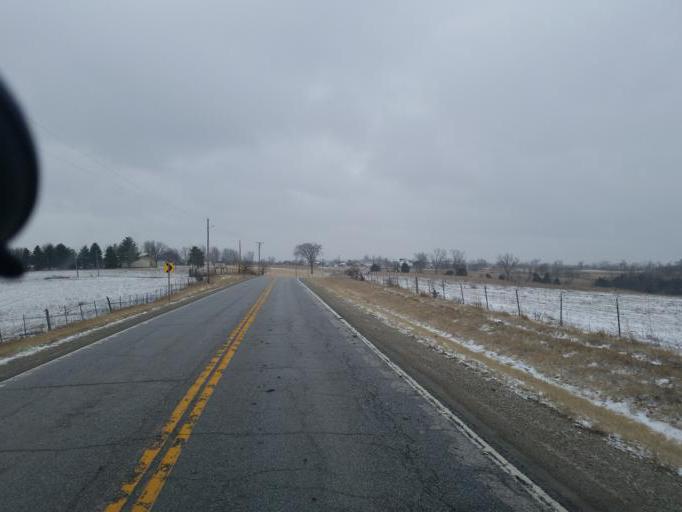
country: US
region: Missouri
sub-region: Putnam County
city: Unionville
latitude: 40.5003
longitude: -93.0097
